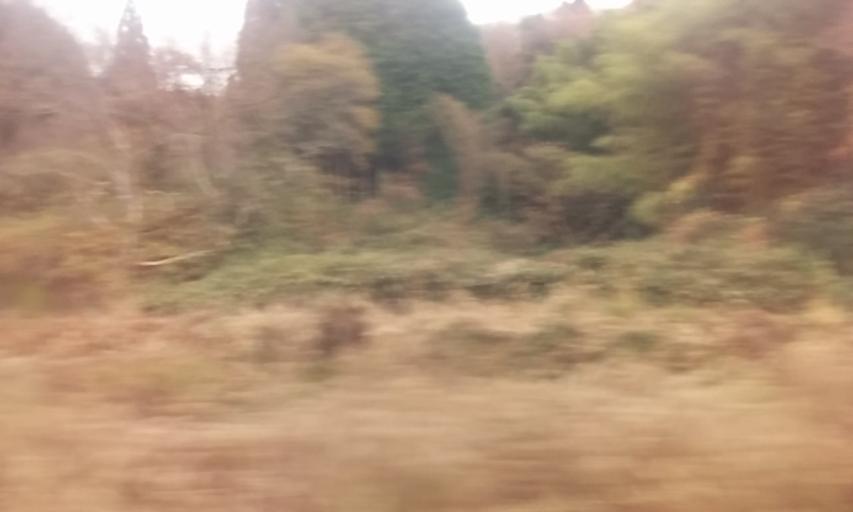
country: JP
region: Gifu
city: Mizunami
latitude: 35.4162
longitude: 137.3168
